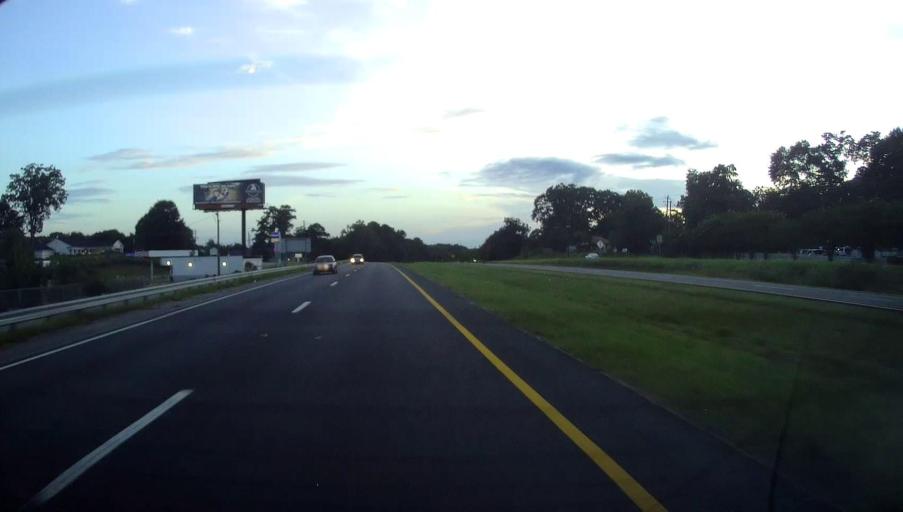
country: US
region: Georgia
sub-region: Muscogee County
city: Columbus
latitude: 32.5121
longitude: -84.9279
